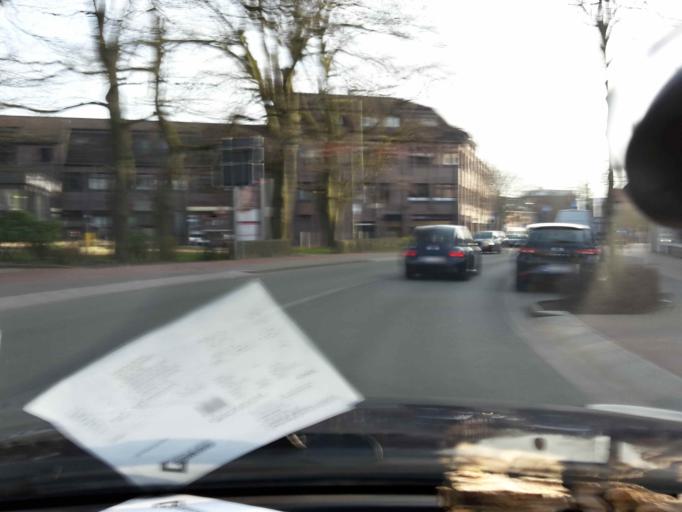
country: DE
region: Lower Saxony
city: Buchholz in der Nordheide
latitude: 53.3303
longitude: 9.8823
